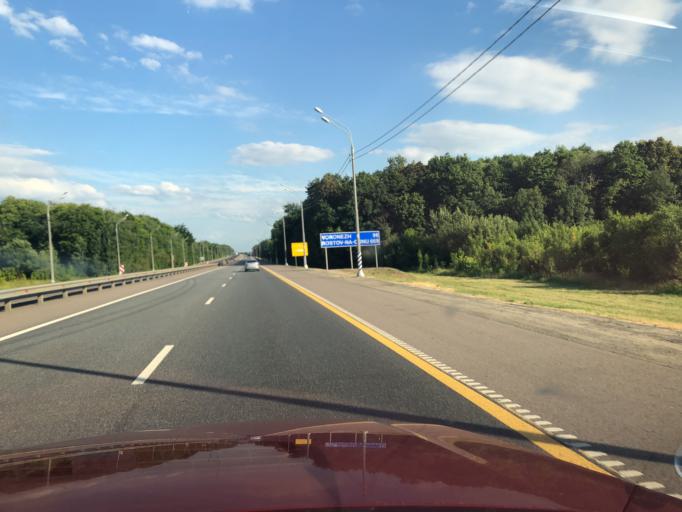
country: RU
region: Lipetsk
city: Zadonsk
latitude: 52.4217
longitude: 38.8349
